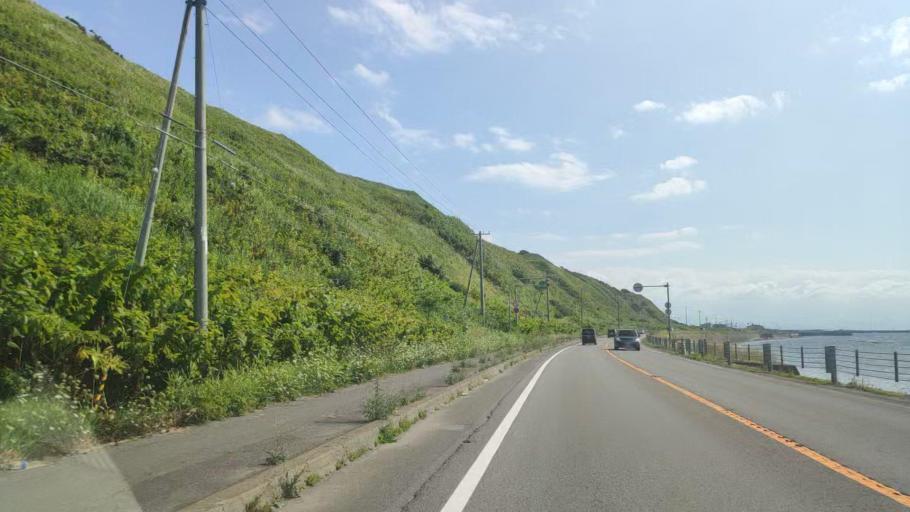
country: JP
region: Hokkaido
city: Rumoi
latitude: 43.9904
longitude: 141.6510
